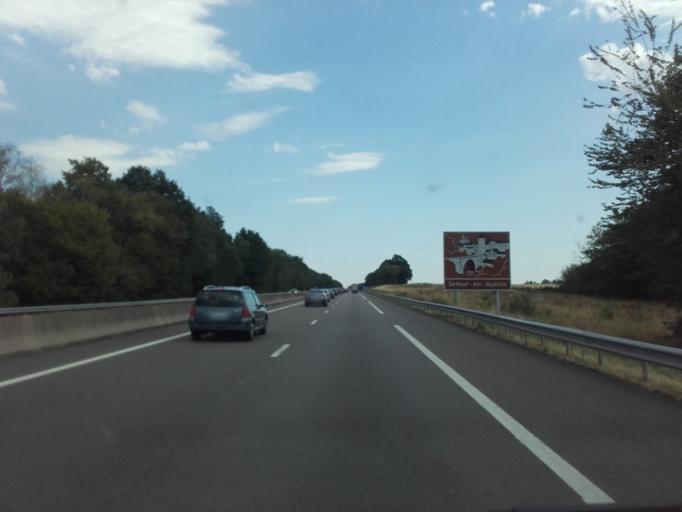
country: FR
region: Bourgogne
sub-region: Departement de la Cote-d'Or
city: Semur-en-Auxois
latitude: 47.4629
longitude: 4.2502
